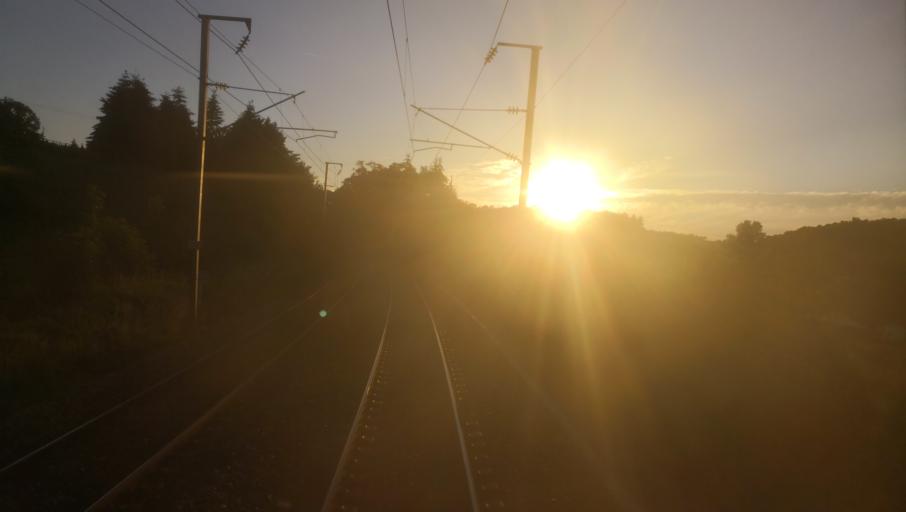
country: FR
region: Haute-Normandie
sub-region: Departement de l'Eure
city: Conches-en-Ouche
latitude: 48.9762
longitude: 0.9728
